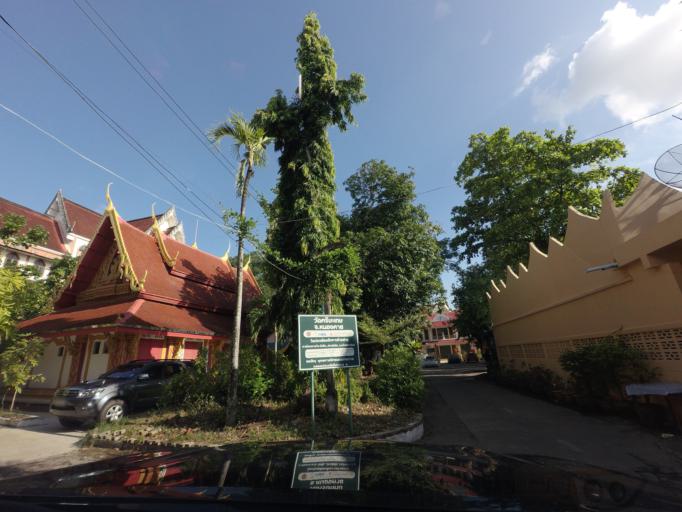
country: TH
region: Nong Khai
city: Nong Khai
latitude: 17.8839
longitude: 102.7479
